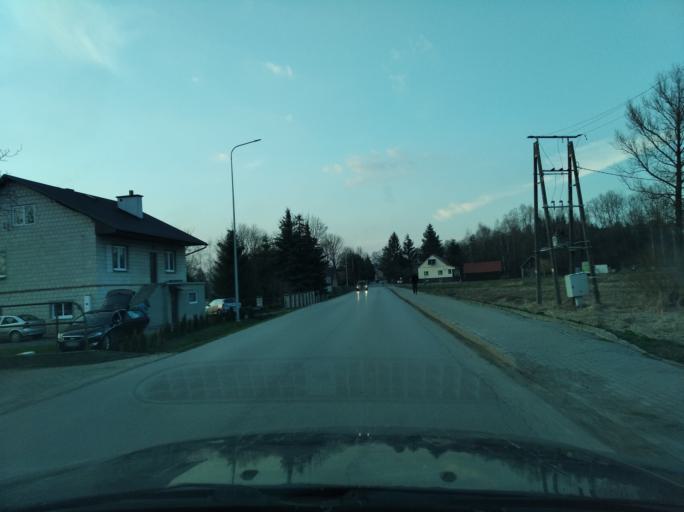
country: PL
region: Subcarpathian Voivodeship
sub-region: Powiat przeworski
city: Zurawiczki
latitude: 50.0296
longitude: 22.5133
